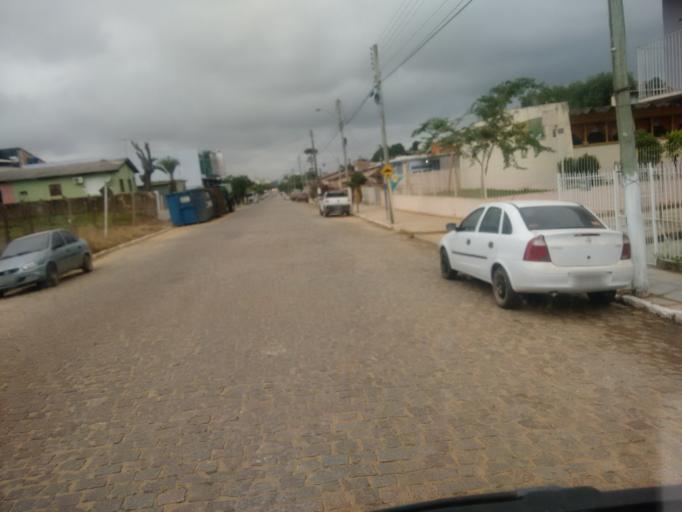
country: BR
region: Rio Grande do Sul
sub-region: Camaqua
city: Camaqua
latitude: -30.8413
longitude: -51.8151
